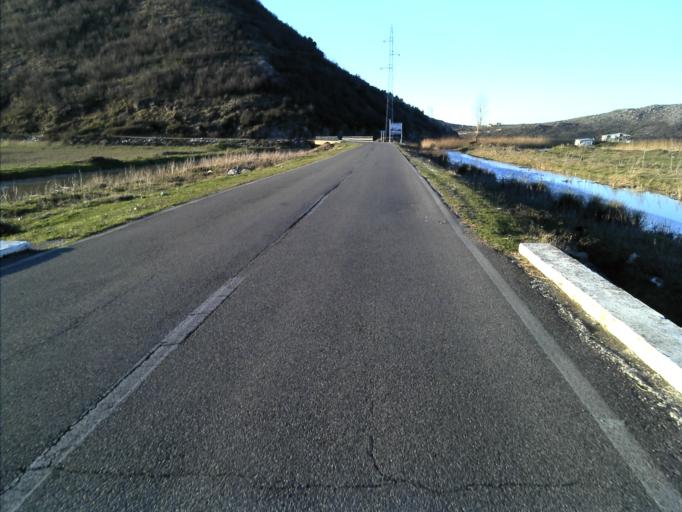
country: AL
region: Shkoder
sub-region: Rrethi i Shkodres
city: Velipoje
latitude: 41.9321
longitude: 19.4420
